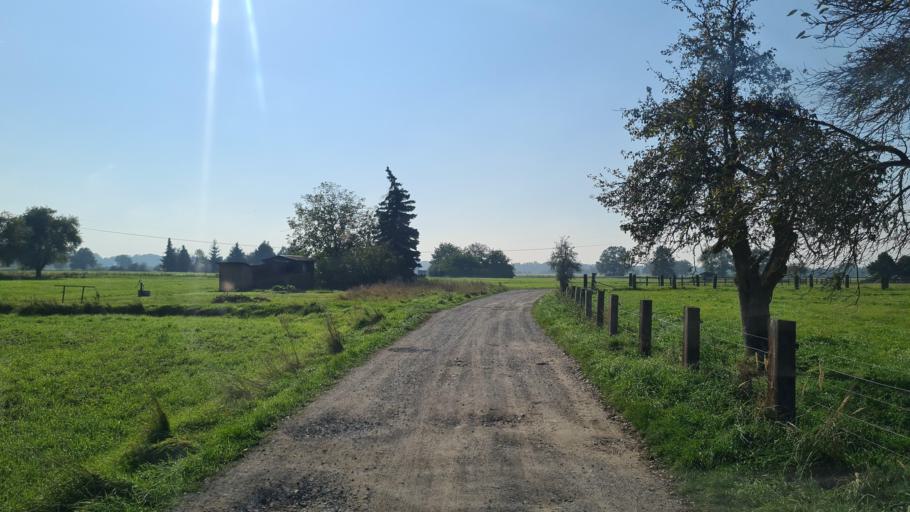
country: DE
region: Brandenburg
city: Luckau
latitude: 51.8455
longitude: 13.7037
